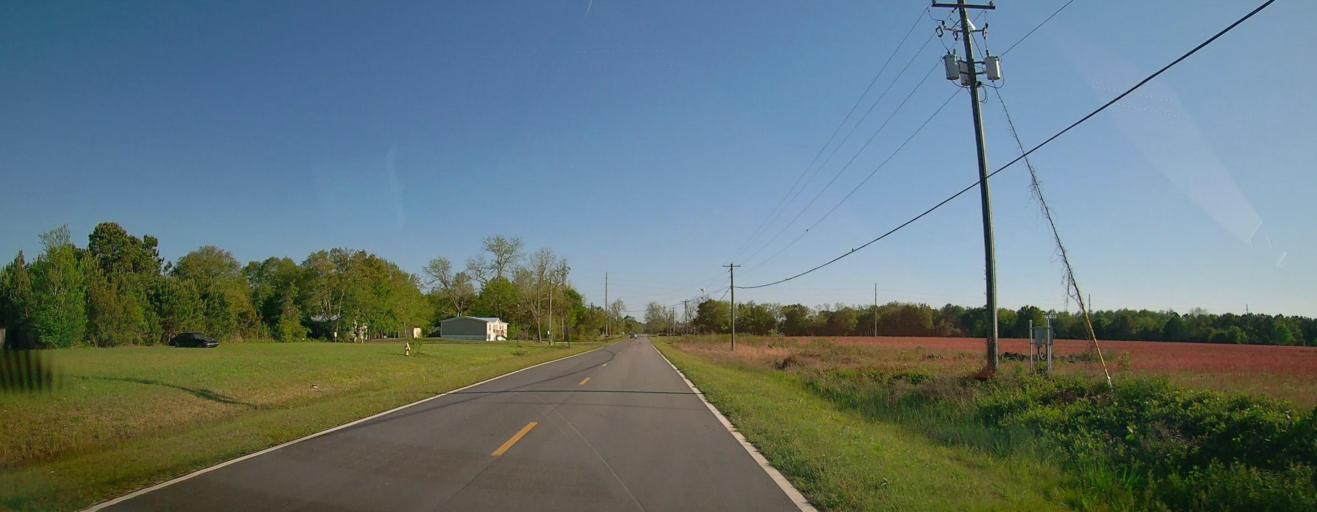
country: US
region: Georgia
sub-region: Ben Hill County
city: Fitzgerald
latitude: 31.7374
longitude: -83.2802
